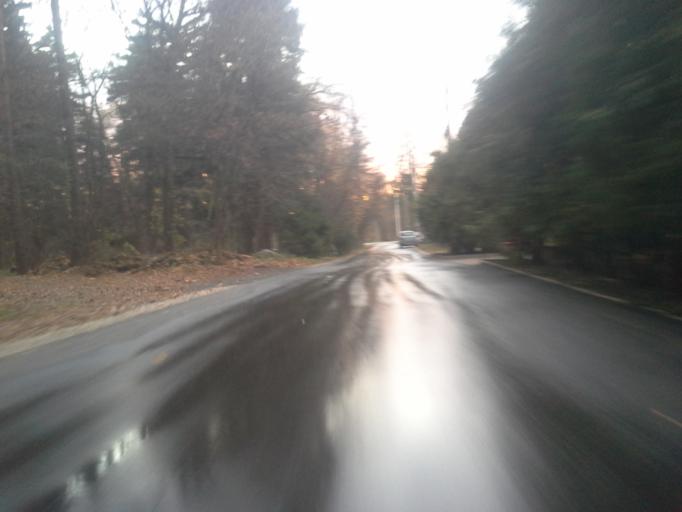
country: RU
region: Moskovskaya
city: Odintsovo
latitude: 55.6395
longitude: 37.2636
